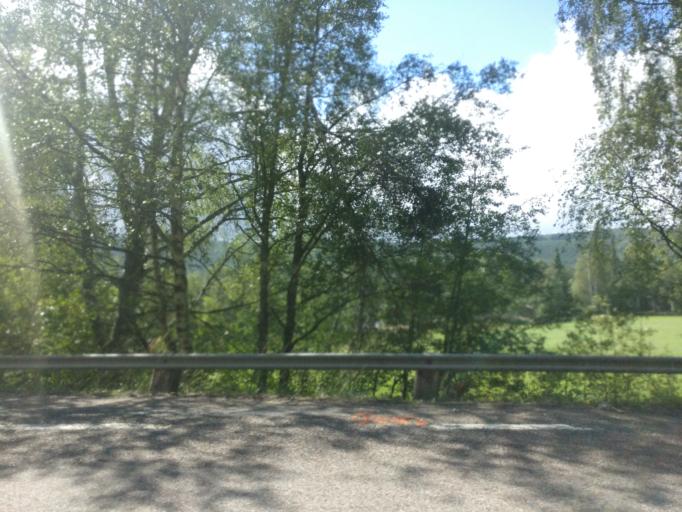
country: SE
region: Vaermland
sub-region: Hagfors Kommun
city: Ekshaerad
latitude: 60.3465
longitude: 13.3444
